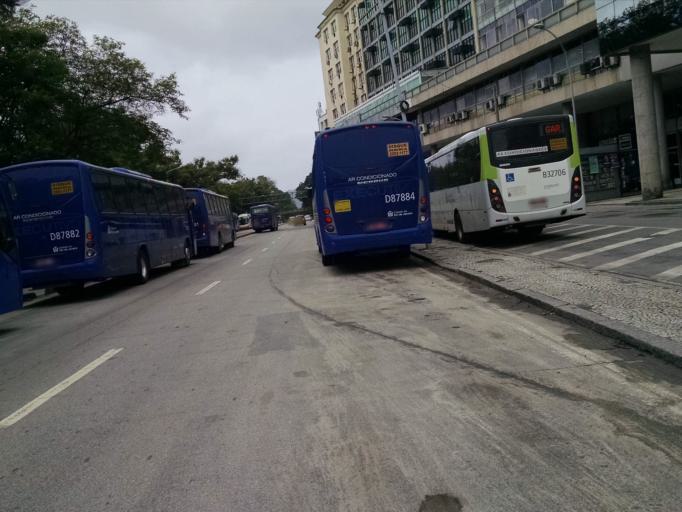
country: BR
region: Rio de Janeiro
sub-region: Rio De Janeiro
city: Rio de Janeiro
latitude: -22.9072
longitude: -43.1685
